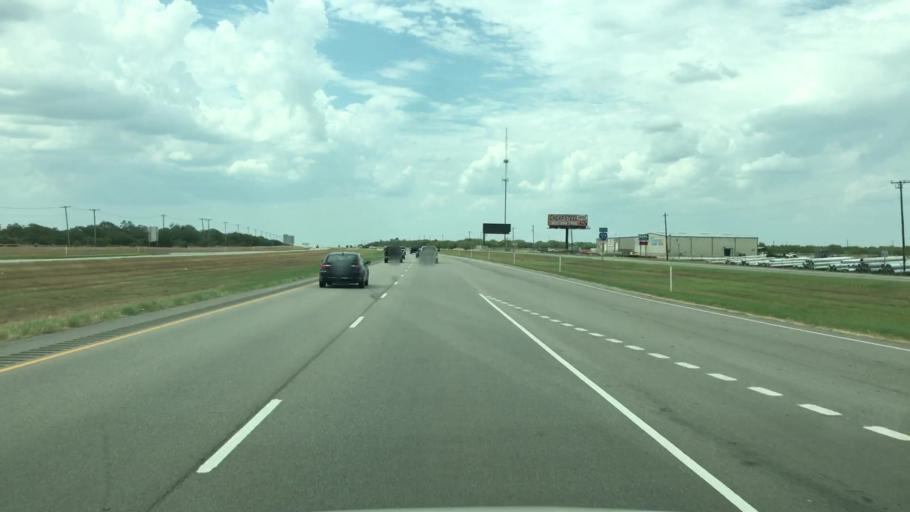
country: US
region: Texas
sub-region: Live Oak County
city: Three Rivers
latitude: 28.4924
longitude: -98.1461
